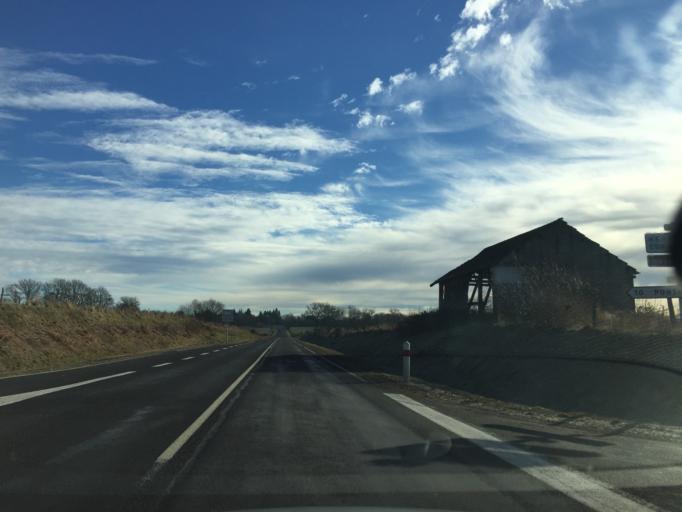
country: FR
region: Limousin
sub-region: Departement de la Creuse
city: Auzances
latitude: 45.8652
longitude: 2.5631
